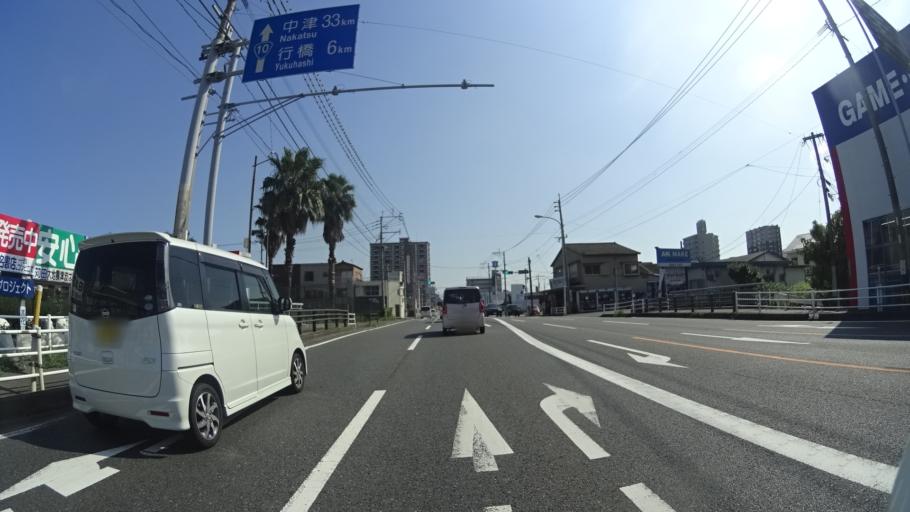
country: JP
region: Fukuoka
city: Kanda
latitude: 33.7844
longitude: 130.9823
